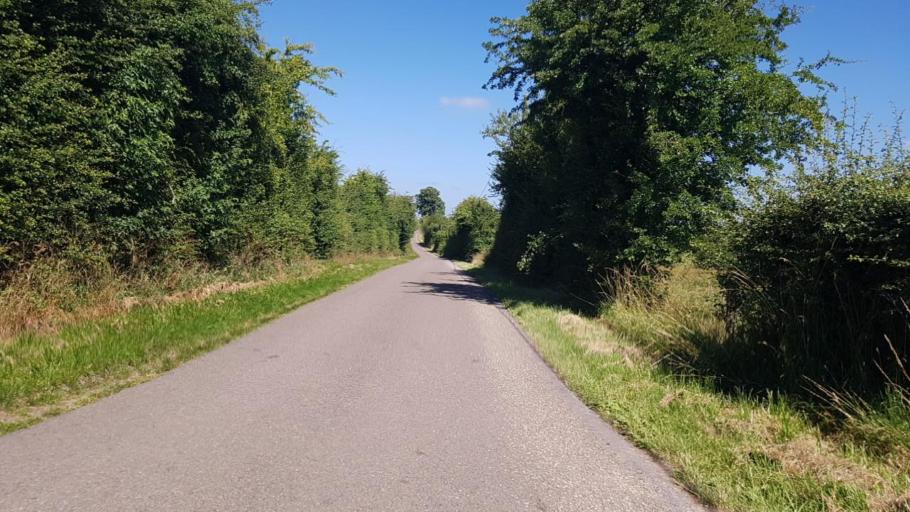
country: BE
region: Wallonia
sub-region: Province du Hainaut
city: Chimay
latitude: 50.0601
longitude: 4.2437
